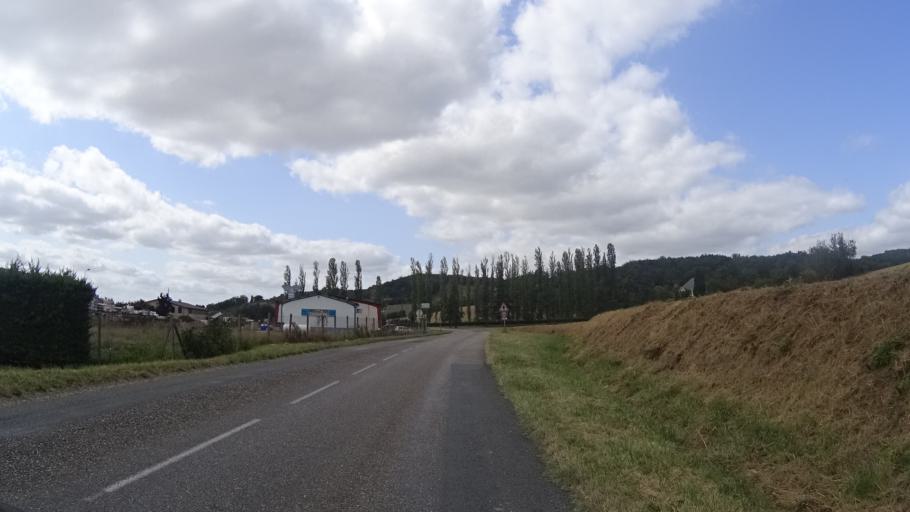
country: FR
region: Aquitaine
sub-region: Departement du Lot-et-Garonne
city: Foulayronnes
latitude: 44.2232
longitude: 0.6568
